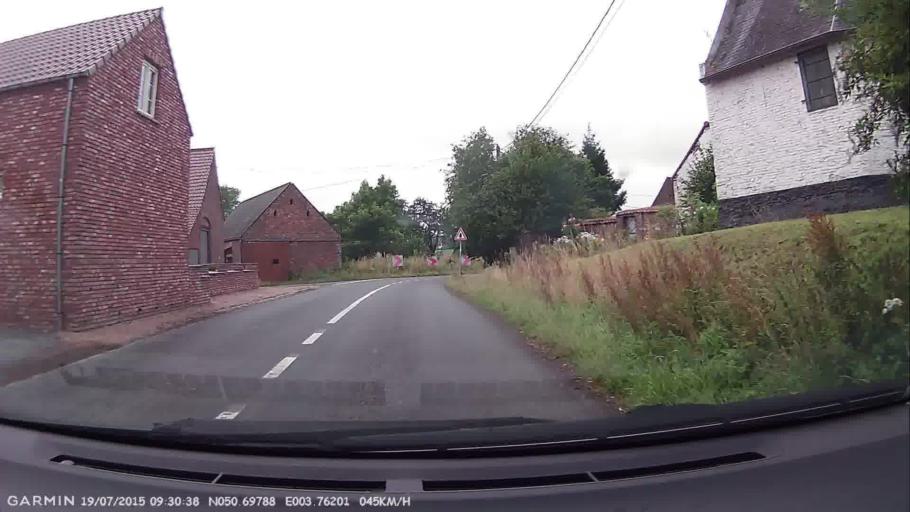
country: BE
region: Wallonia
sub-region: Province du Hainaut
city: Flobecq
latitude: 50.6979
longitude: 3.7620
